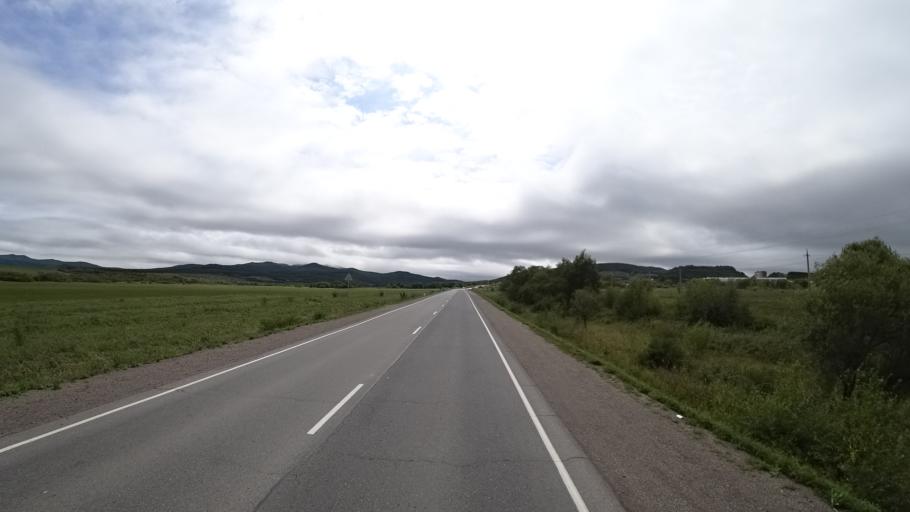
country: RU
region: Primorskiy
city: Monastyrishche
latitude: 44.1742
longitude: 132.4413
